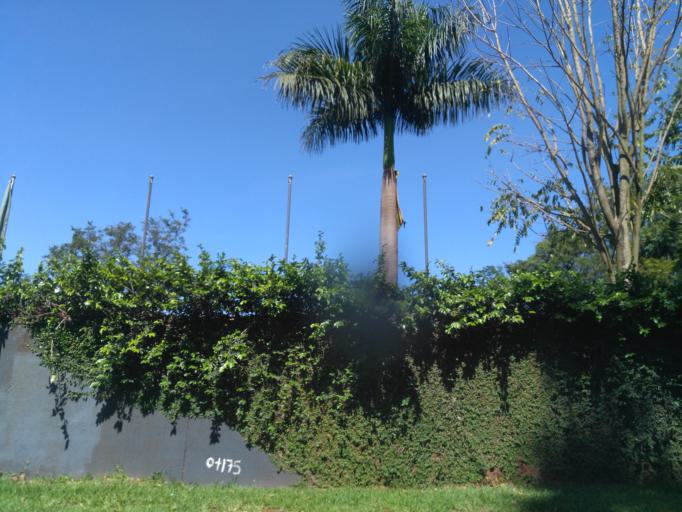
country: UG
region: Central Region
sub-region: Kampala District
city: Kampala
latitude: 0.3221
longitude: 32.5833
